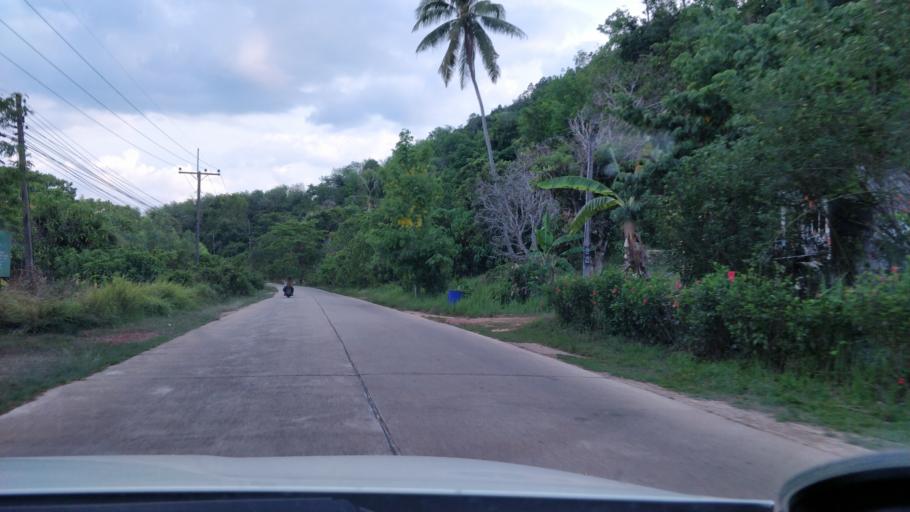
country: TH
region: Krabi
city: Saladan
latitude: 7.5811
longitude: 99.0674
